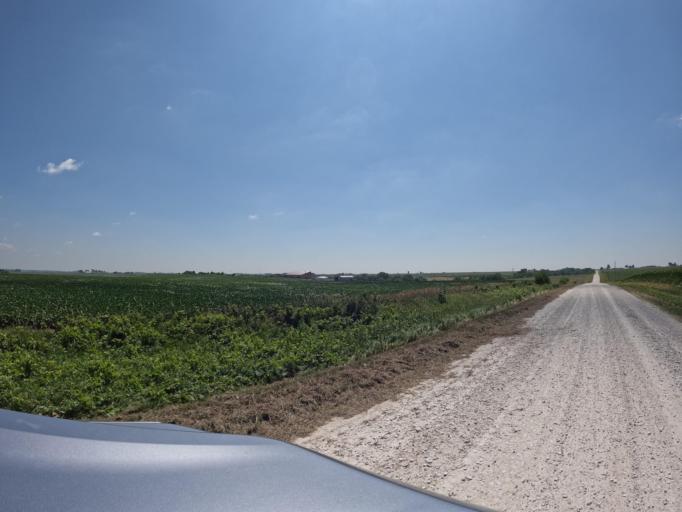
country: US
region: Iowa
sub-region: Keokuk County
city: Sigourney
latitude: 41.2809
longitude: -92.2381
